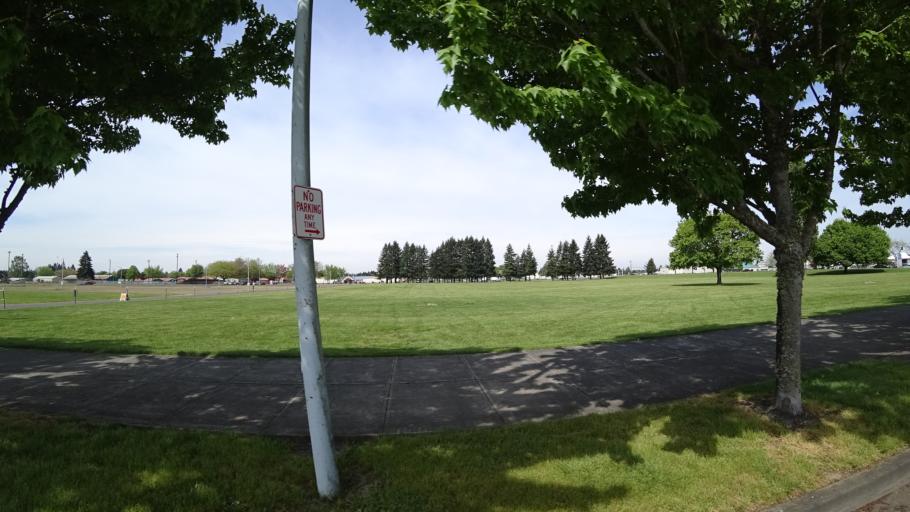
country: US
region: Oregon
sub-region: Washington County
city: Hillsboro
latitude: 45.5309
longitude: -122.9467
